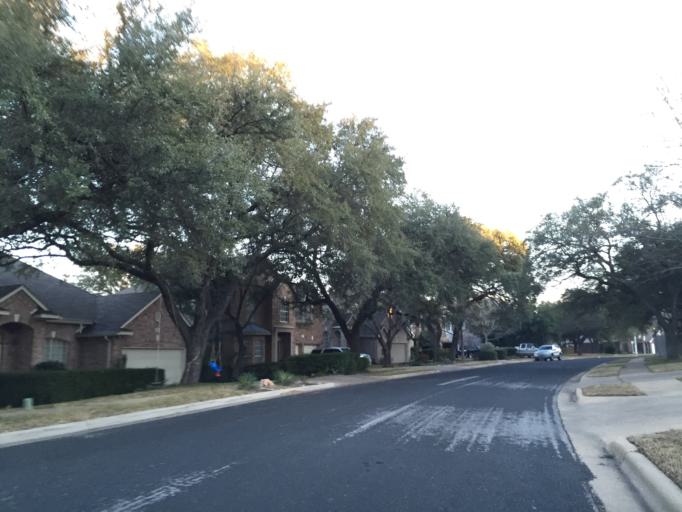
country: US
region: Texas
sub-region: Williamson County
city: Jollyville
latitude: 30.4418
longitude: -97.7629
